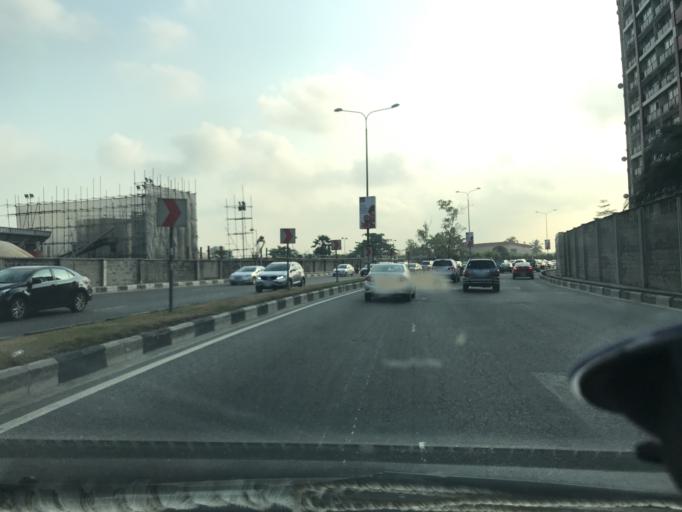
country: NG
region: Lagos
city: Ikoyi
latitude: 6.4404
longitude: 3.4336
